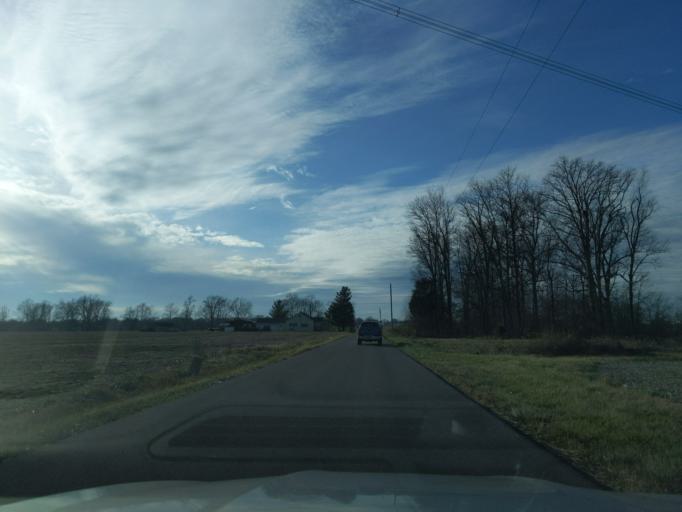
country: US
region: Indiana
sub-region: Decatur County
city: Westport
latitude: 39.1835
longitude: -85.5562
